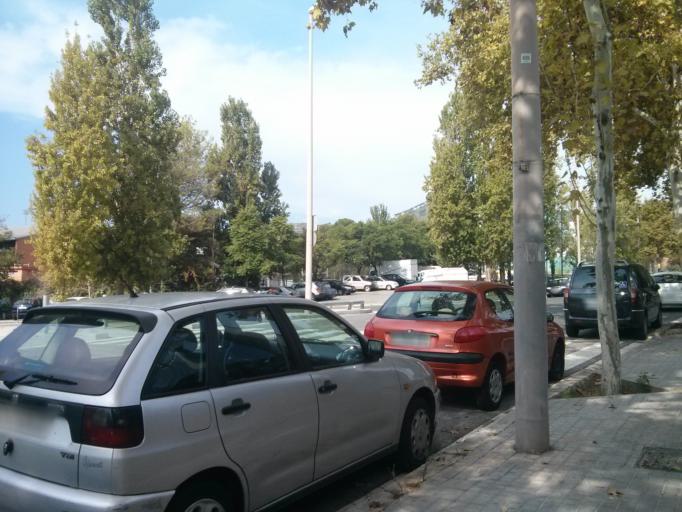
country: ES
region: Catalonia
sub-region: Provincia de Barcelona
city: Esplugues de Llobregat
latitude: 41.3802
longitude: 2.1080
